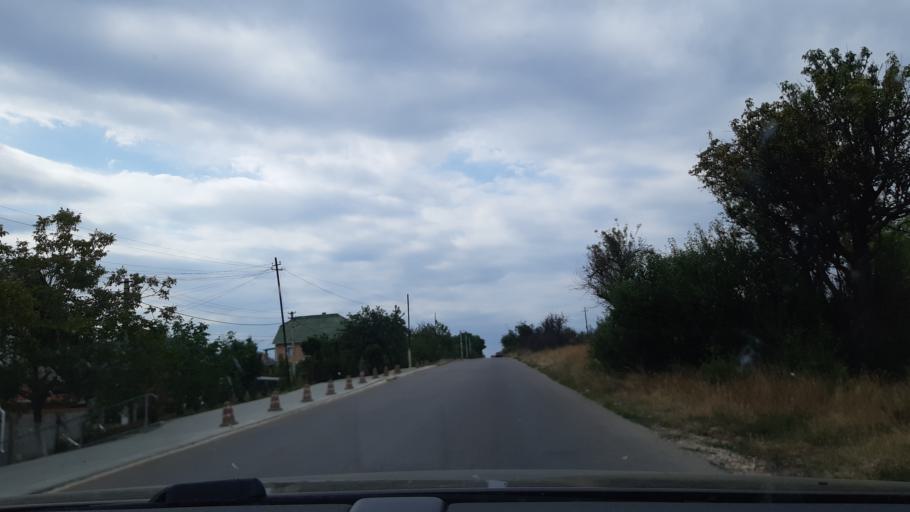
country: MD
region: Chisinau
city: Vatra
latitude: 47.0437
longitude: 28.7475
